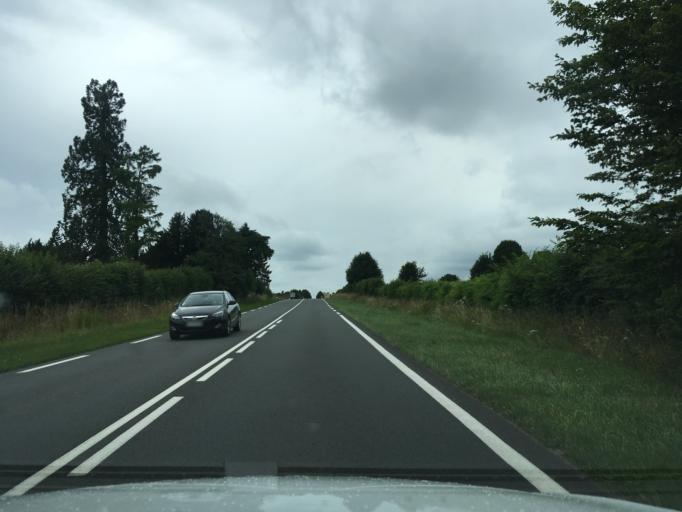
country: FR
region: Picardie
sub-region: Departement de l'Aisne
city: La Capelle
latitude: 49.9713
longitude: 3.9321
